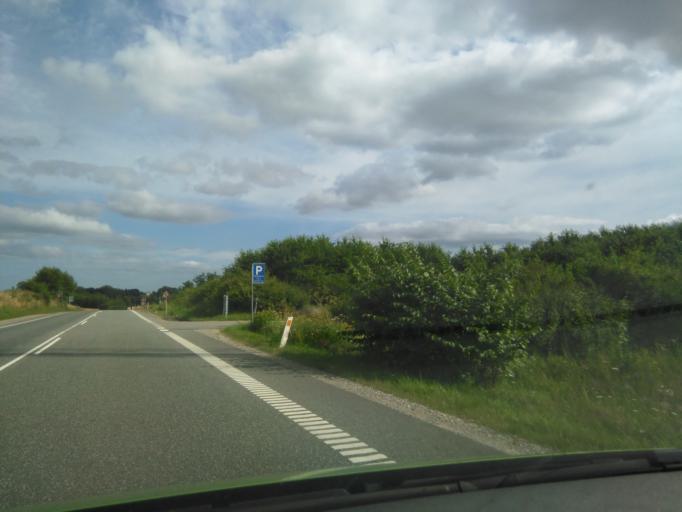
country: DK
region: Central Jutland
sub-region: Arhus Kommune
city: Kolt
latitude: 56.1079
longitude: 10.0533
